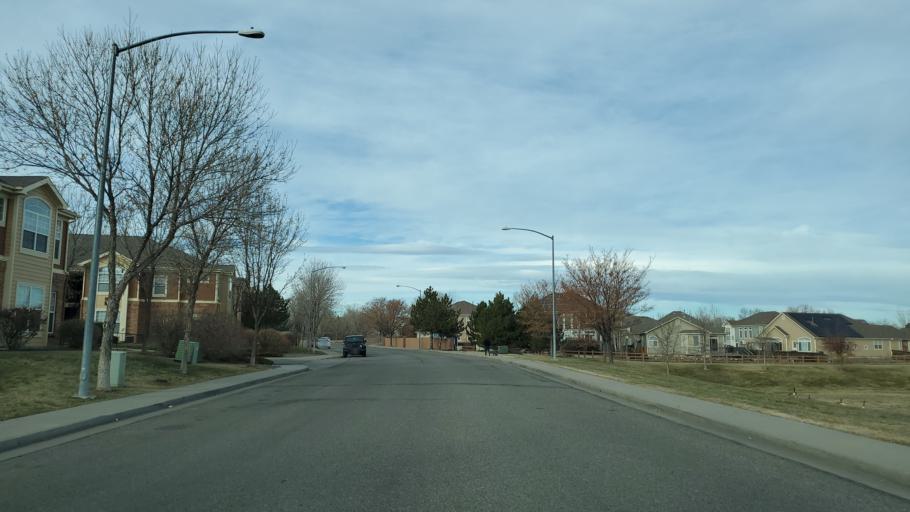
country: US
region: Colorado
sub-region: Adams County
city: Northglenn
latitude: 39.9159
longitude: -104.9476
